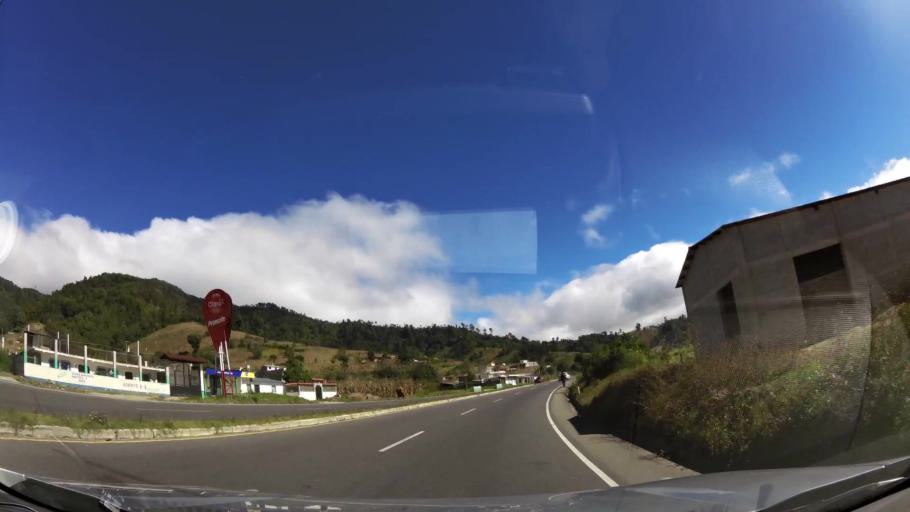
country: GT
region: Solola
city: Solola
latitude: 14.8246
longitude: -91.1982
